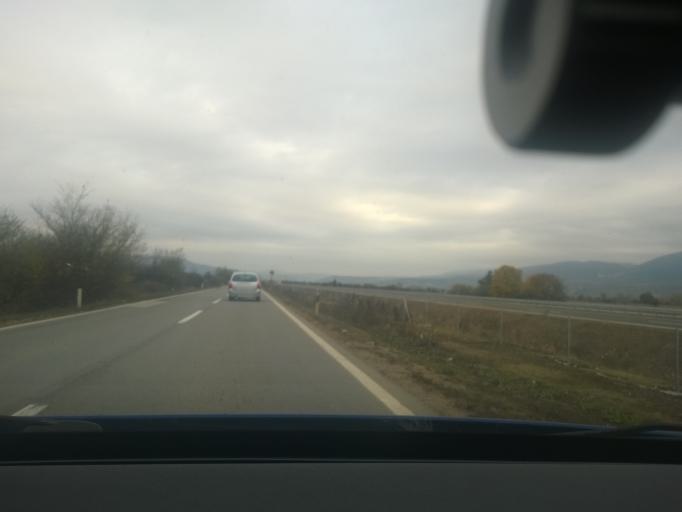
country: RS
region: Central Serbia
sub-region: Pirotski Okrug
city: Pirot
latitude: 43.0978
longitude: 22.6451
